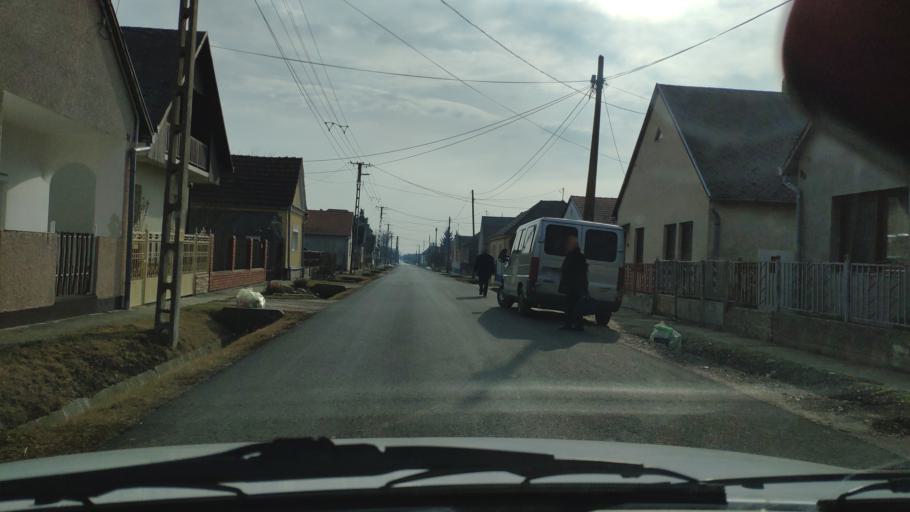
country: HU
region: Zala
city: Murakeresztur
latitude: 46.4372
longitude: 16.9077
